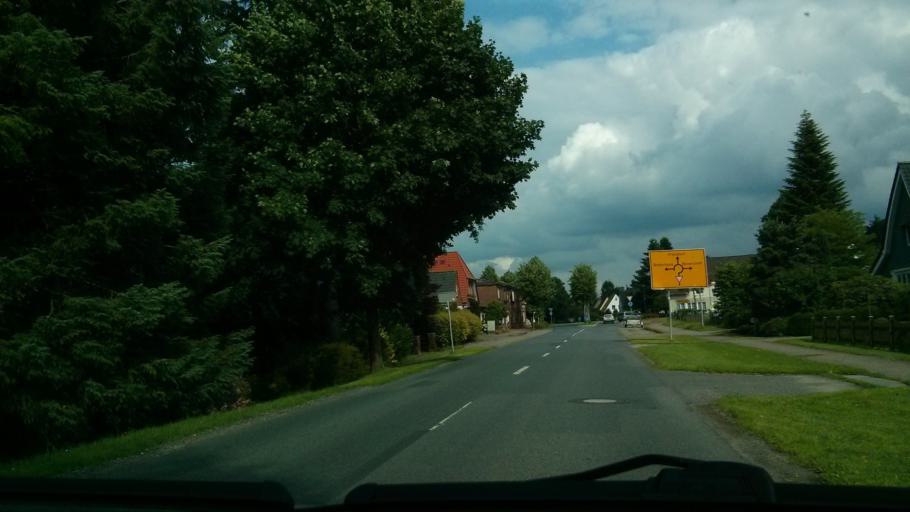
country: DE
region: Lower Saxony
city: Kohlen
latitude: 53.5083
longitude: 8.8558
